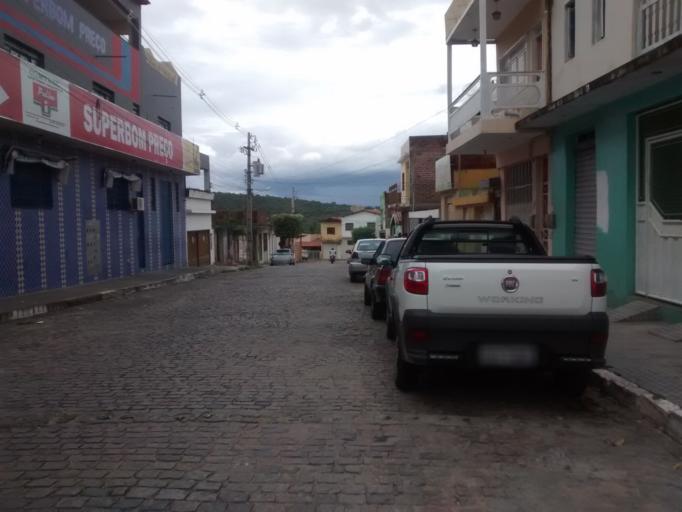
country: BR
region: Bahia
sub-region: Brumado
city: Brumado
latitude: -14.2098
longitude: -41.6730
